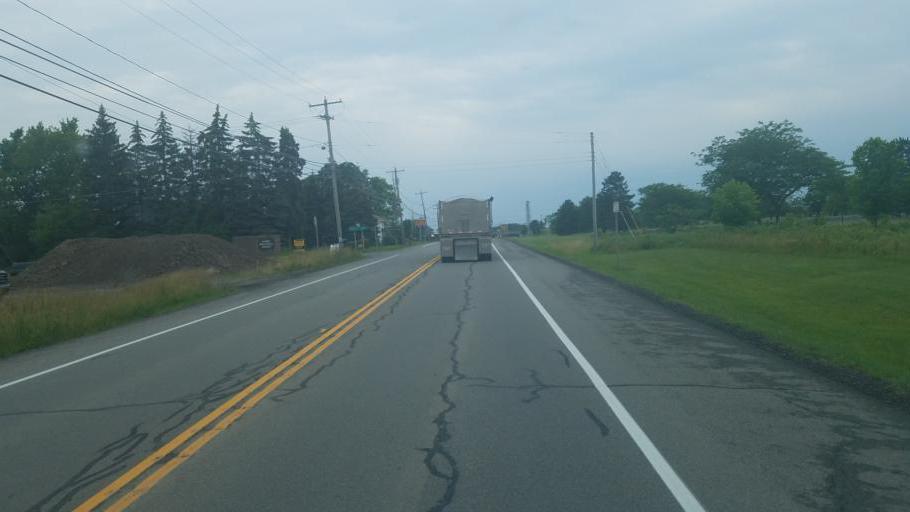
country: US
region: New York
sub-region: Niagara County
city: Lewiston
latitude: 43.1300
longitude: -79.0121
